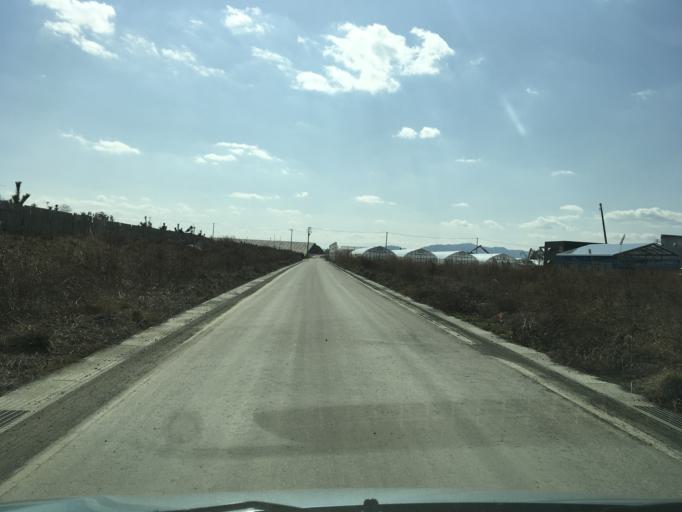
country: JP
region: Iwate
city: Ofunato
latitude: 38.8265
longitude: 141.5919
